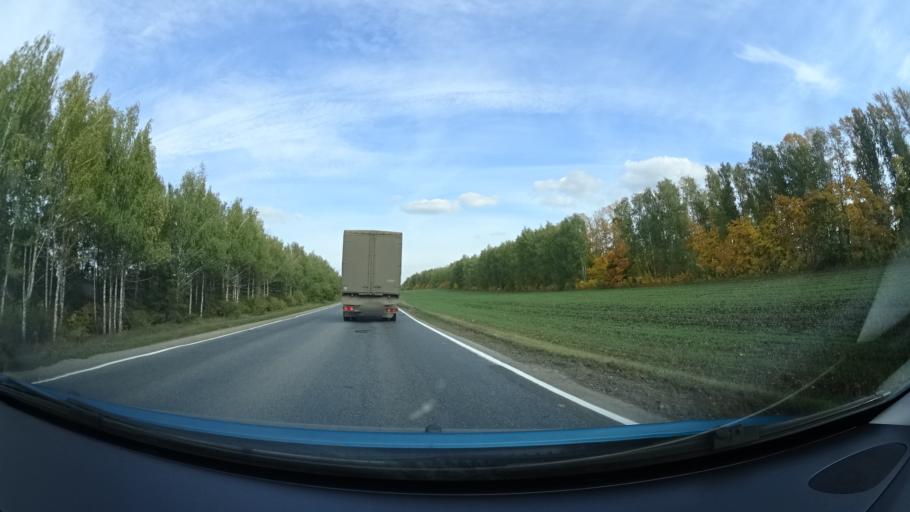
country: RU
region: Bashkortostan
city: Kandry
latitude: 54.5499
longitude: 54.1713
